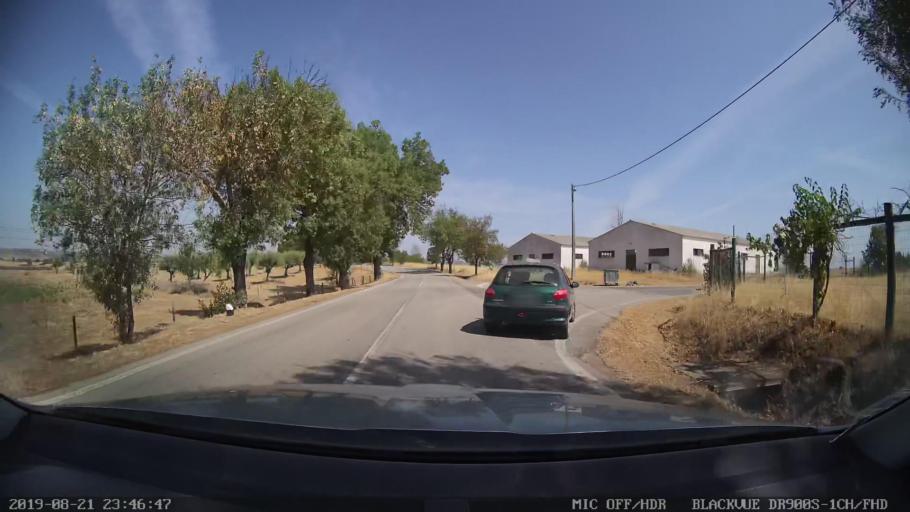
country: PT
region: Castelo Branco
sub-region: Idanha-A-Nova
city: Idanha-a-Nova
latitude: 39.8446
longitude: -7.2564
